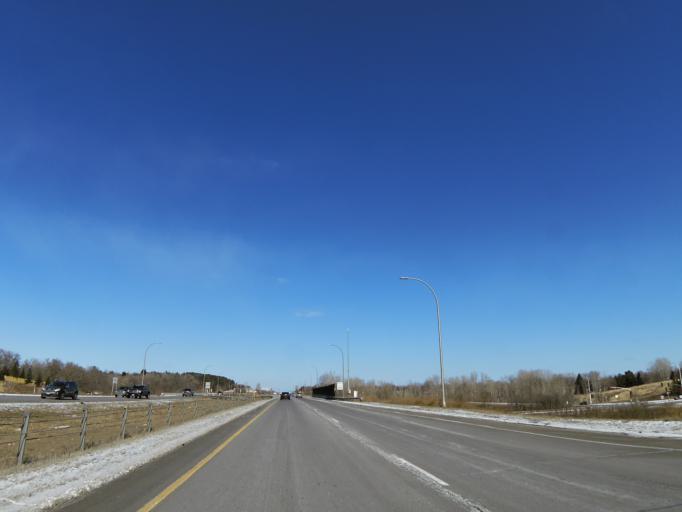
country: US
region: Minnesota
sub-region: Scott County
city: Savage
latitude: 44.8066
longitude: -93.3981
